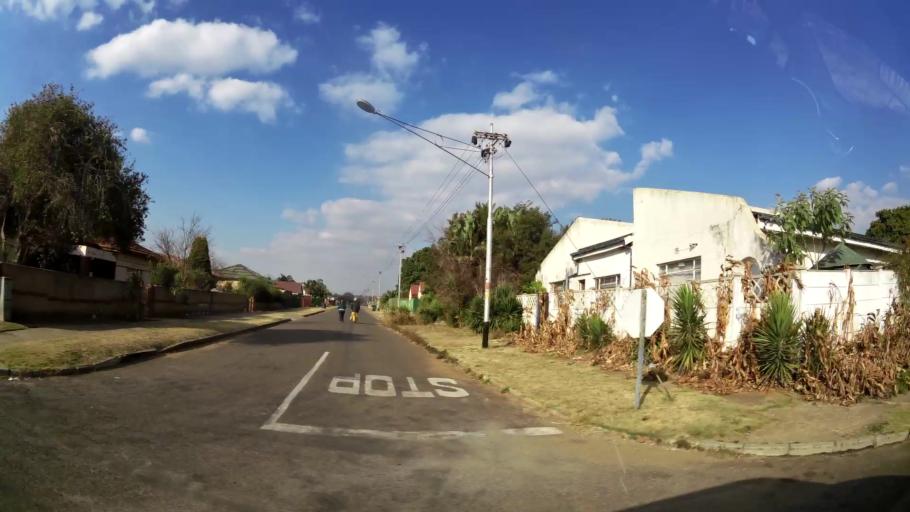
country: ZA
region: Gauteng
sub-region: West Rand District Municipality
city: Krugersdorp
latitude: -26.0923
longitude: 27.7441
